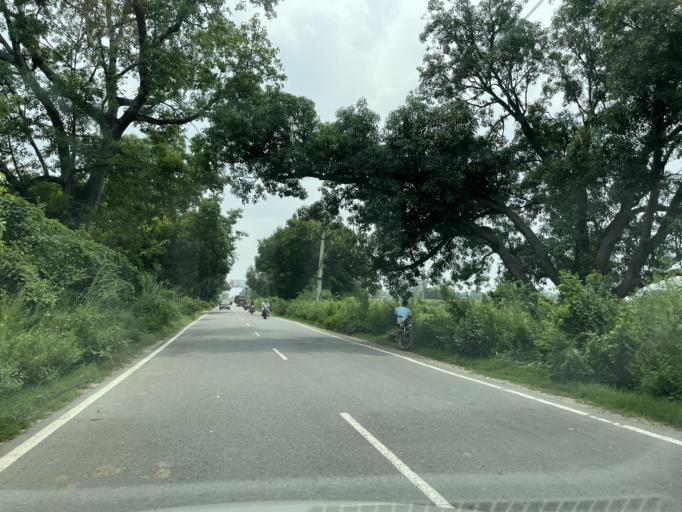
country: IN
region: Uttar Pradesh
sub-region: Bijnor
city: Najibabad
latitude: 29.5779
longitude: 78.3385
